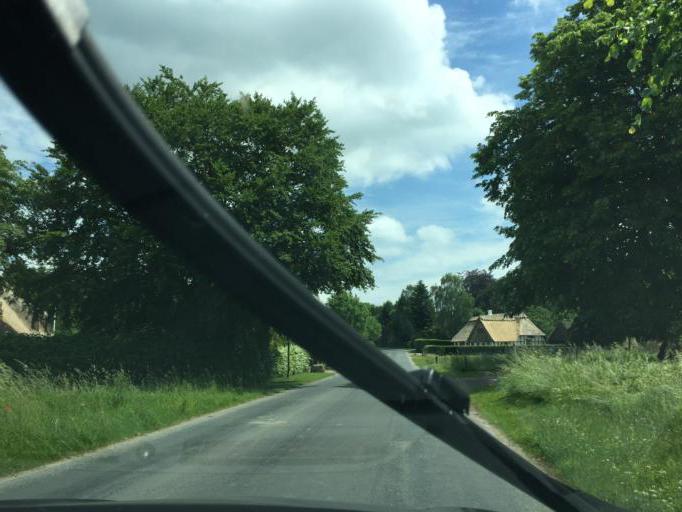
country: DK
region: South Denmark
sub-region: Faaborg-Midtfyn Kommune
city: Ringe
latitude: 55.1967
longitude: 10.4916
